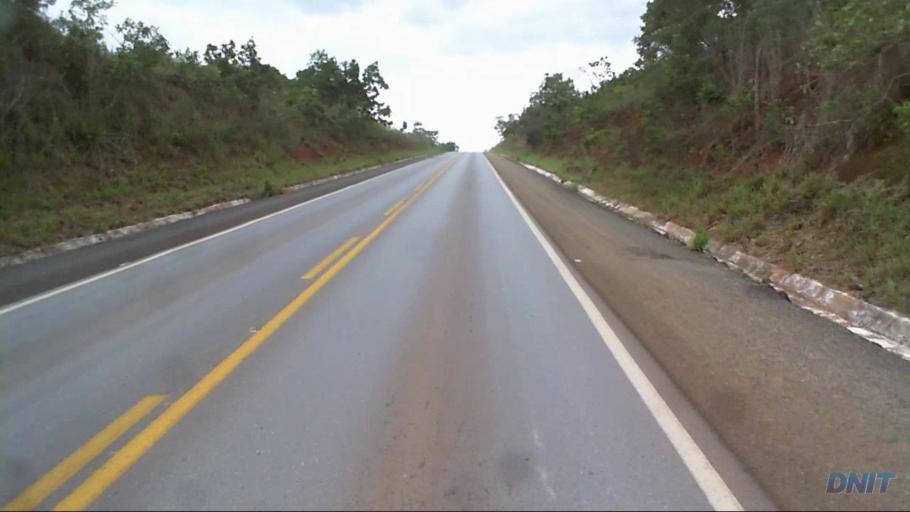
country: BR
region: Goias
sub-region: Uruacu
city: Uruacu
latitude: -14.7567
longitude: -49.0680
